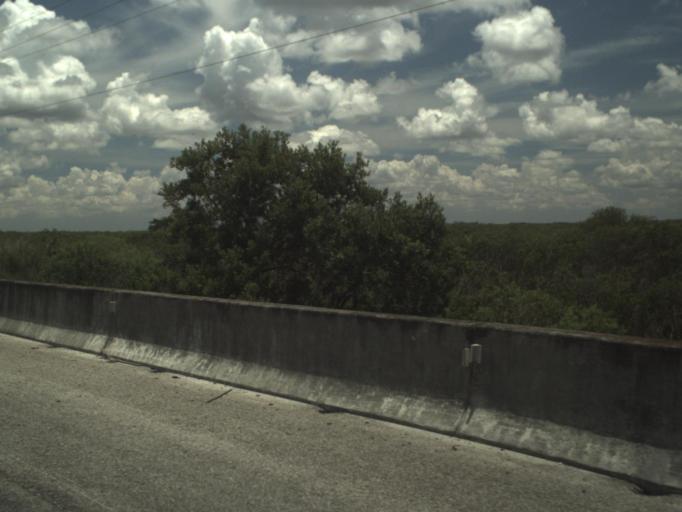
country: US
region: Florida
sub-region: Broward County
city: Weston
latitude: 26.1512
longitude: -80.7316
